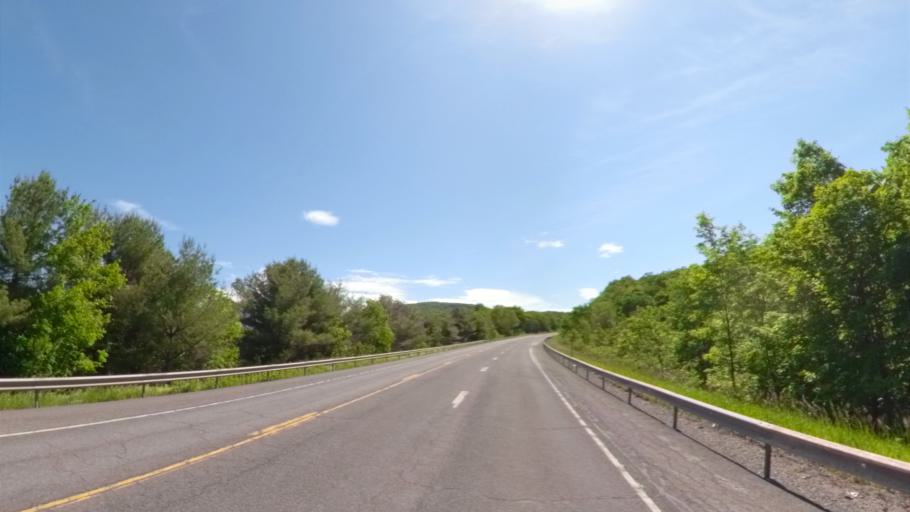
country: US
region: New York
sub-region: Delaware County
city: Stamford
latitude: 42.1516
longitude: -74.5081
